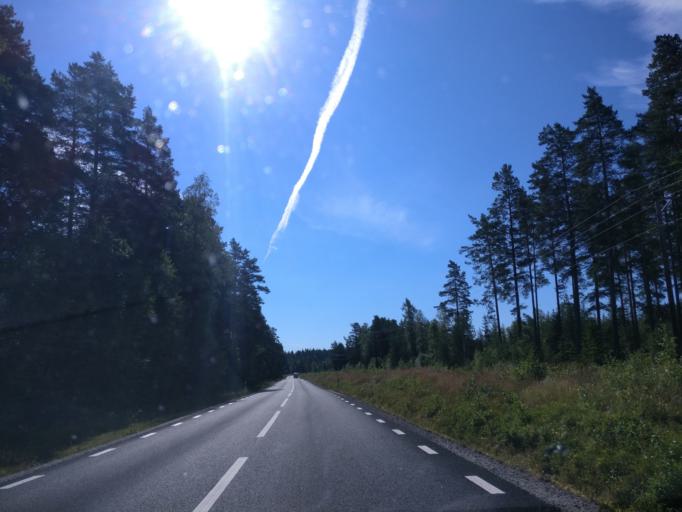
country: SE
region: Vaermland
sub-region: Hagfors Kommun
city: Hagfors
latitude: 60.0368
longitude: 13.8278
